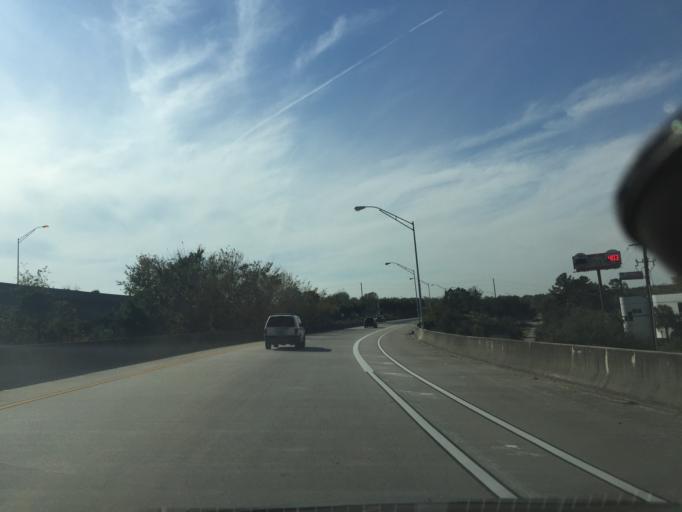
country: US
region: Georgia
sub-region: Chatham County
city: Savannah
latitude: 32.0719
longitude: -81.1052
